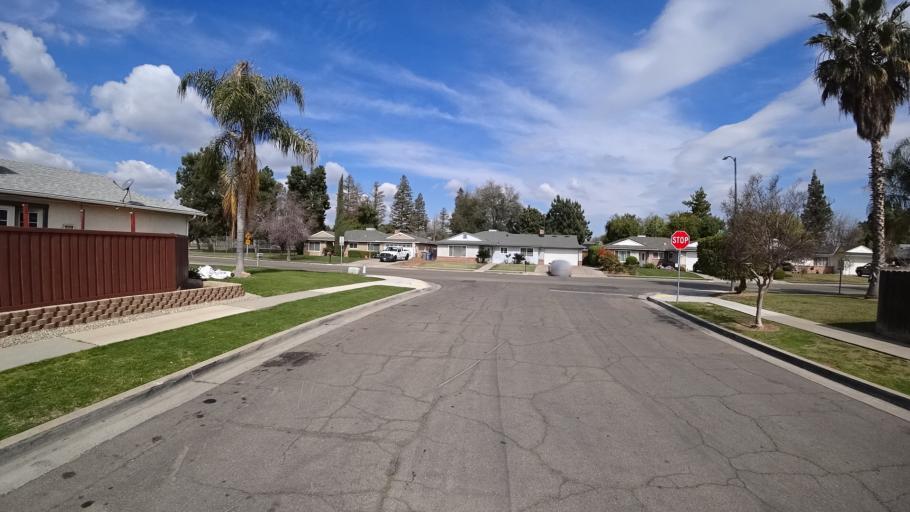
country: US
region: California
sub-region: Fresno County
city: Fresno
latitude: 36.8152
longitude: -119.8508
